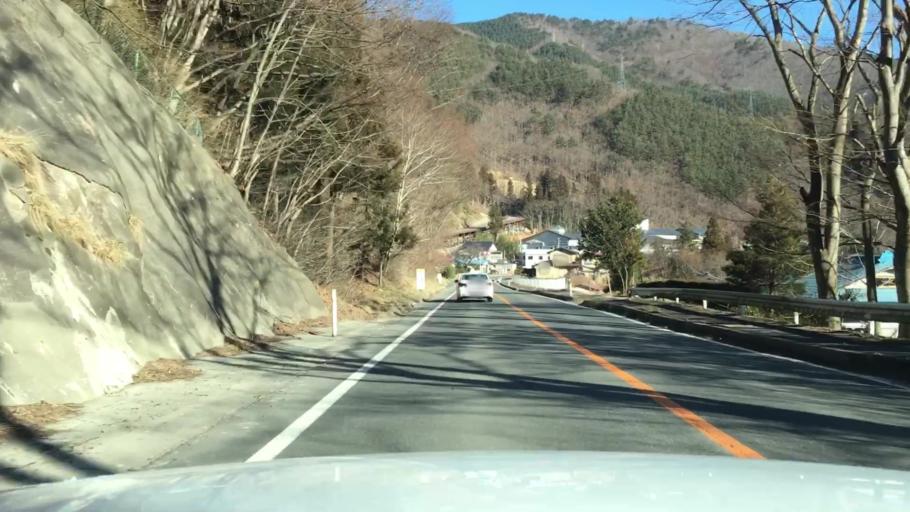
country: JP
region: Iwate
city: Miyako
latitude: 39.5963
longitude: 141.6768
